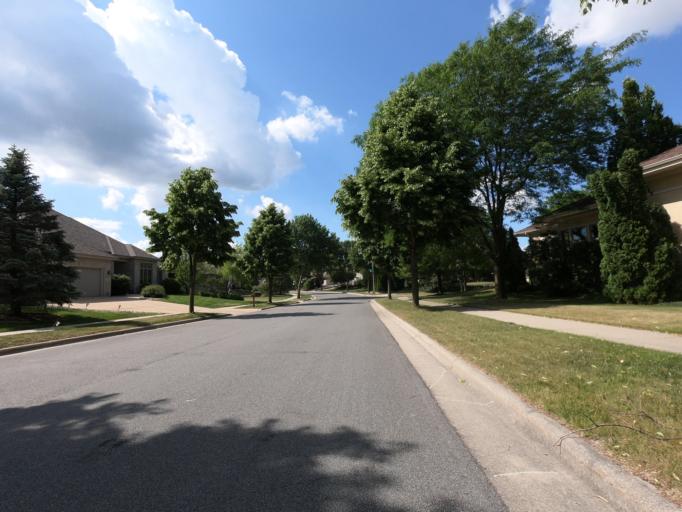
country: US
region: Wisconsin
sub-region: Dane County
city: Middleton
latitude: 43.0767
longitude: -89.5431
